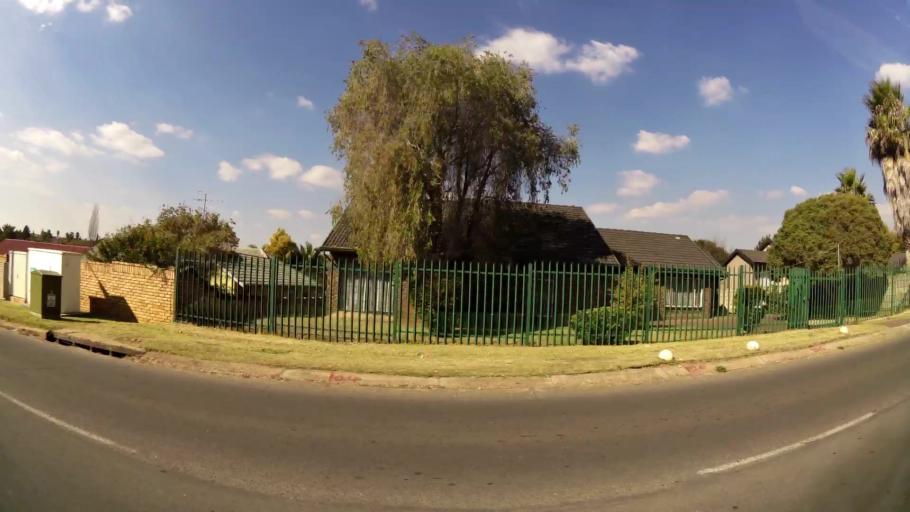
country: ZA
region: Gauteng
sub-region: Ekurhuleni Metropolitan Municipality
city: Tembisa
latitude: -26.0694
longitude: 28.2489
